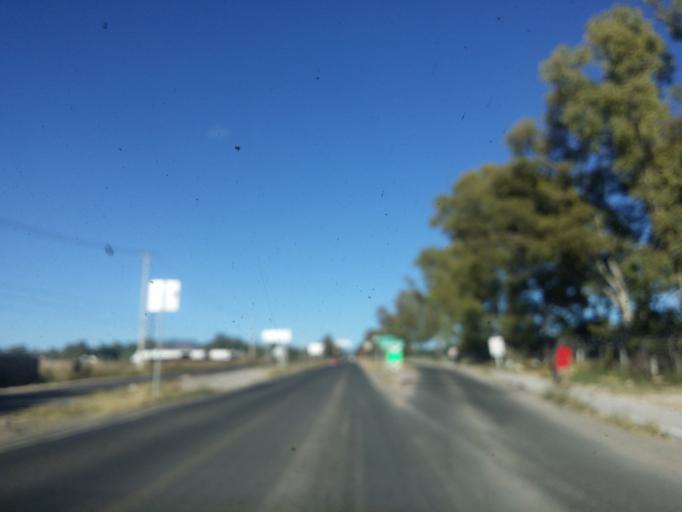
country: MX
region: Guanajuato
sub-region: Silao de la Victoria
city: El Refugio de los Sauces
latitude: 21.0269
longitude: -101.5351
